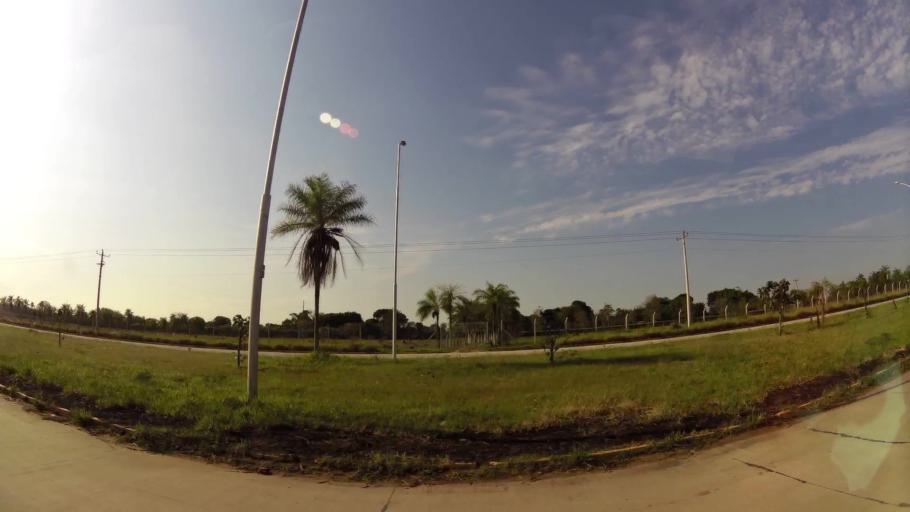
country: BO
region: Santa Cruz
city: Santa Cruz de la Sierra
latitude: -17.6963
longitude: -63.1228
